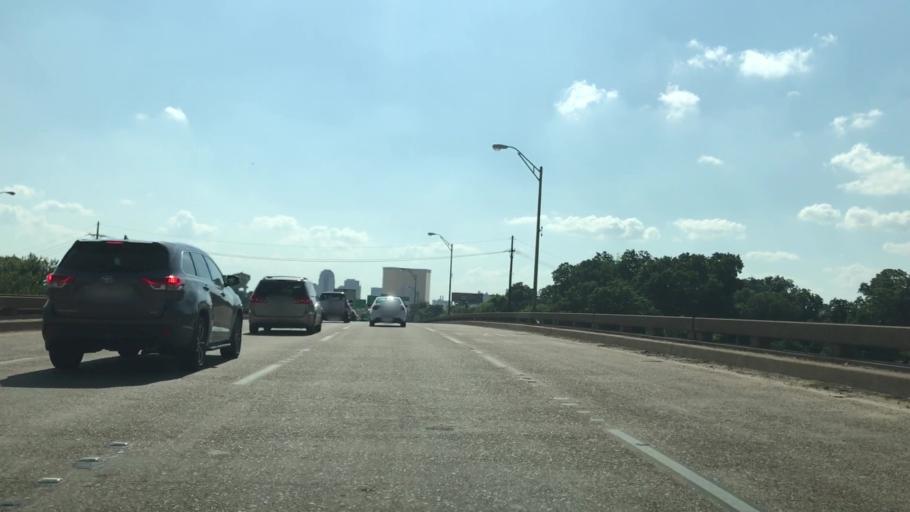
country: US
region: Louisiana
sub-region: Bossier Parish
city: Bossier City
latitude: 32.5139
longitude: -93.7212
